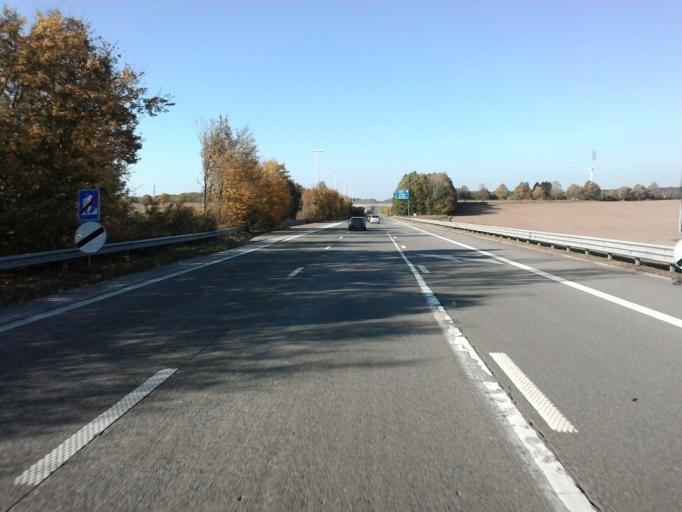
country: BE
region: Wallonia
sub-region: Province de Namur
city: Ciney
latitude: 50.2617
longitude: 5.0417
